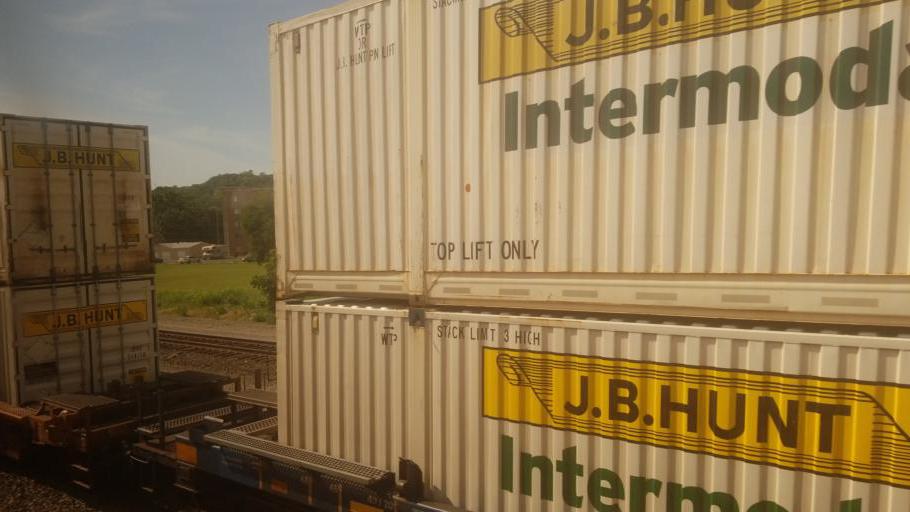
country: US
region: Kansas
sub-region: Johnson County
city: Mission
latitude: 39.0779
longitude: -94.6650
